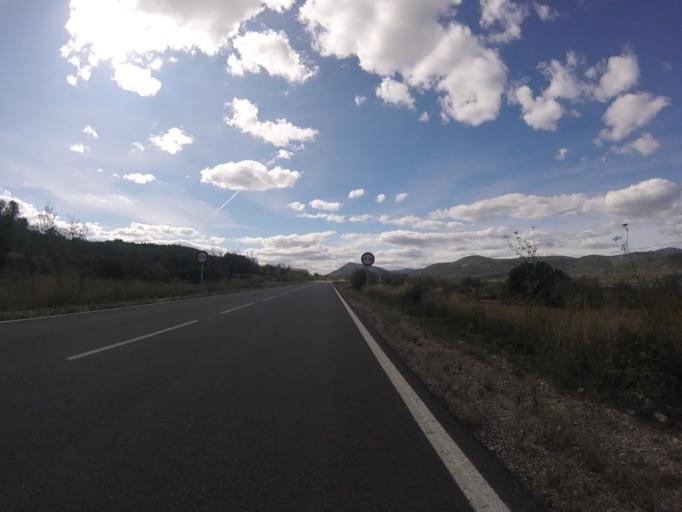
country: ES
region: Valencia
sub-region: Provincia de Castello
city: Cati
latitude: 40.4257
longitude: 0.0862
